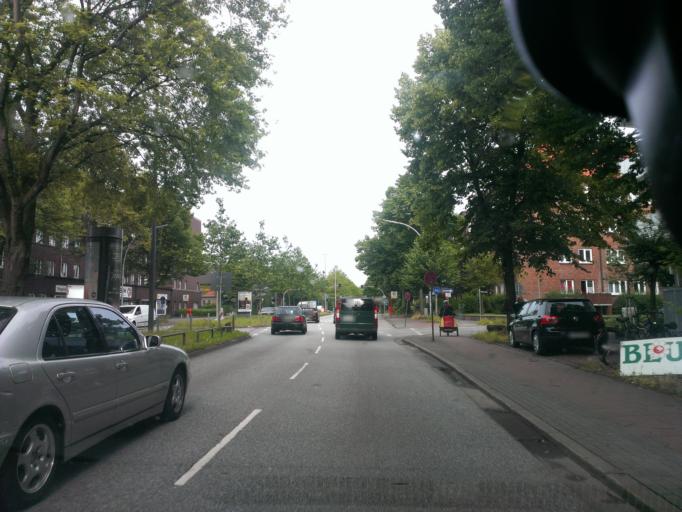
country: DE
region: Hamburg
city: Marienthal
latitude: 53.5602
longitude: 10.0635
